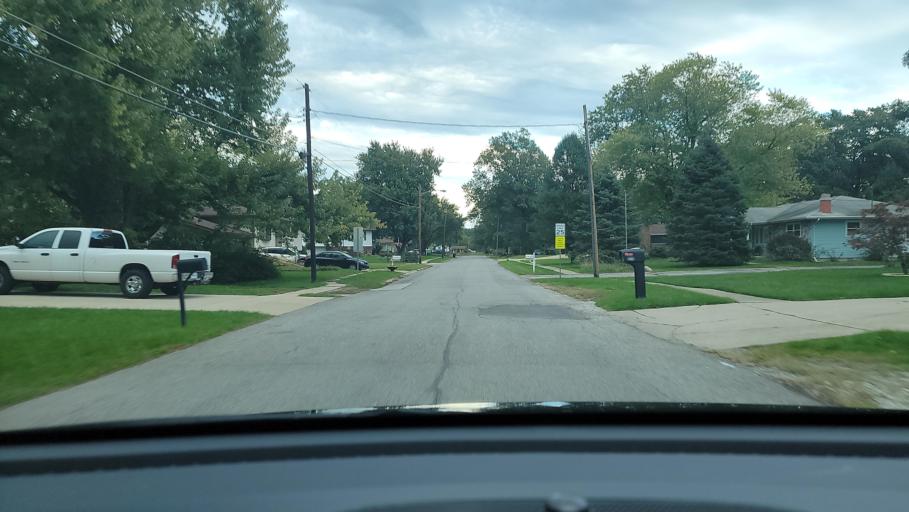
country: US
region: Indiana
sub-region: Porter County
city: Portage
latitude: 41.5686
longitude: -87.1784
